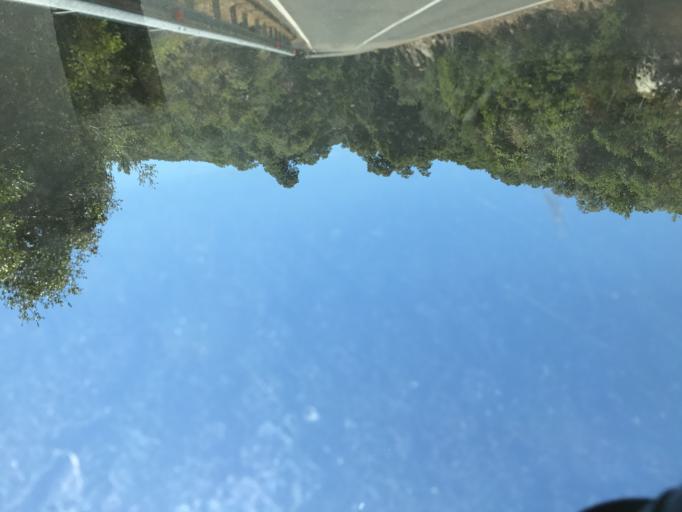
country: IT
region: Sardinia
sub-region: Provincia di Olbia-Tempio
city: Calangianus
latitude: 40.9097
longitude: 9.2029
